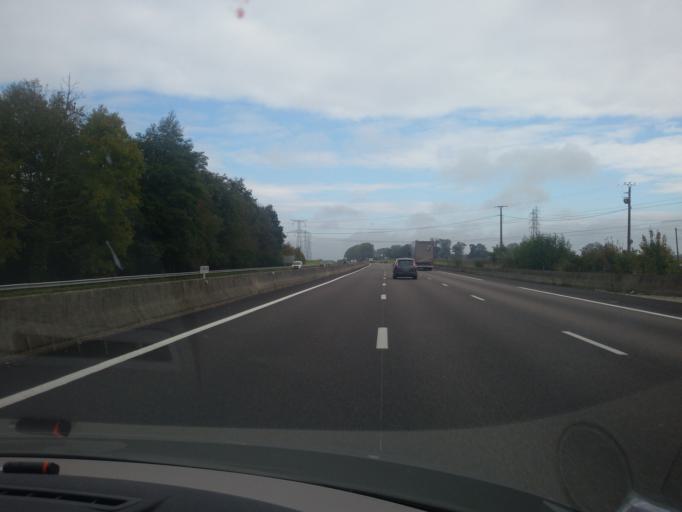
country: FR
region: Haute-Normandie
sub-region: Departement de l'Eure
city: Hauville
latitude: 49.3700
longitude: 0.7387
